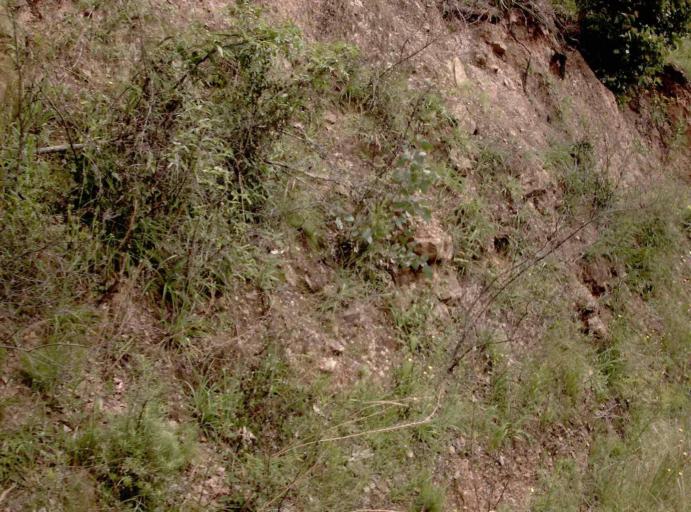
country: AU
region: Victoria
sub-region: Wellington
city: Heyfield
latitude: -37.7309
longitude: 146.6699
